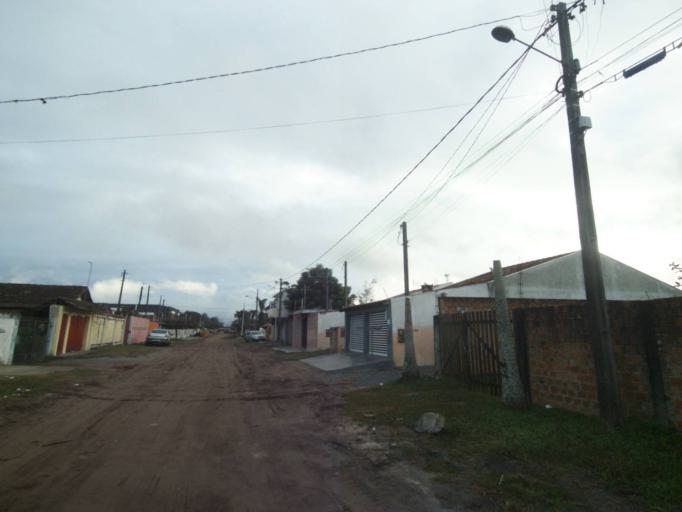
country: BR
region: Parana
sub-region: Paranagua
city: Paranagua
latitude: -25.5715
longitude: -48.5715
